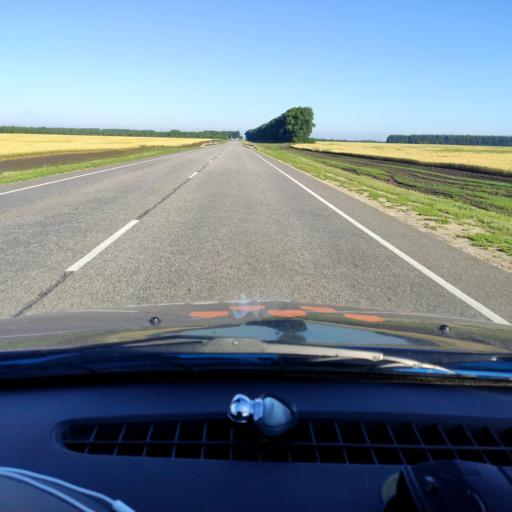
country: RU
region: Orjol
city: Pokrovskoye
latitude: 52.6350
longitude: 36.6897
